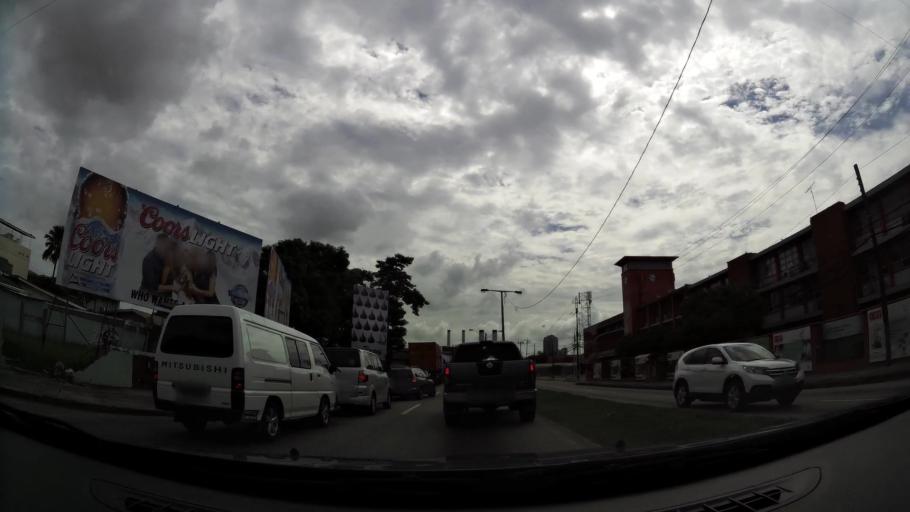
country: TT
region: City of Port of Spain
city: Port-of-Spain
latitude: 10.6588
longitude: -61.5228
